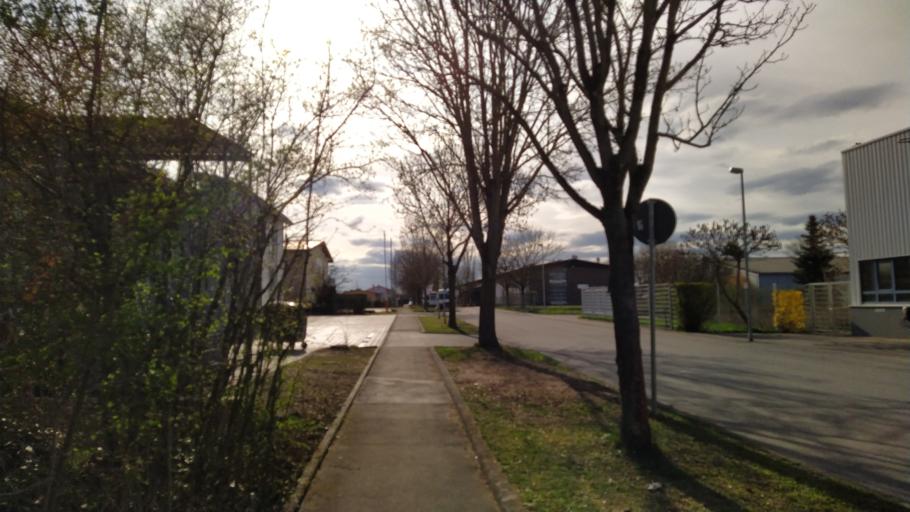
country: DE
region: Baden-Wuerttemberg
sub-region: Tuebingen Region
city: Tuebingen
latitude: 48.4953
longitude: 8.9956
